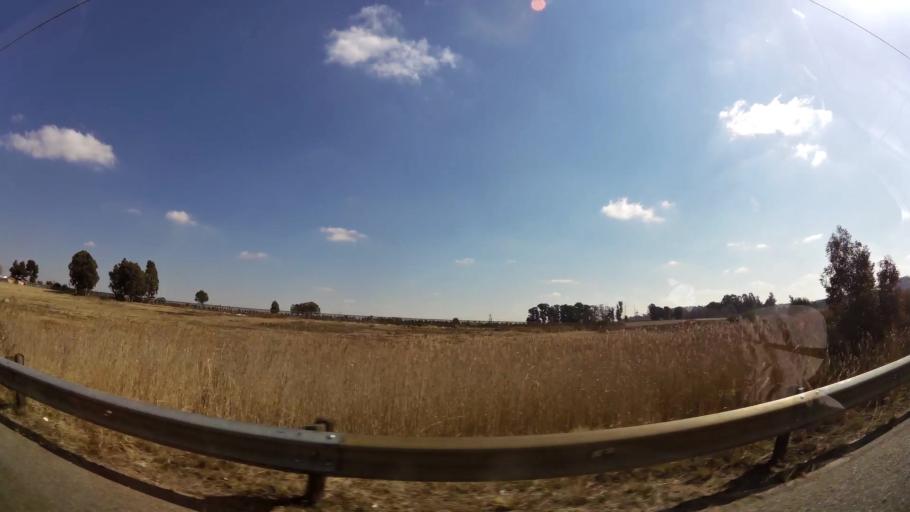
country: ZA
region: Gauteng
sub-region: West Rand District Municipality
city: Randfontein
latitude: -26.1539
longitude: 27.7626
